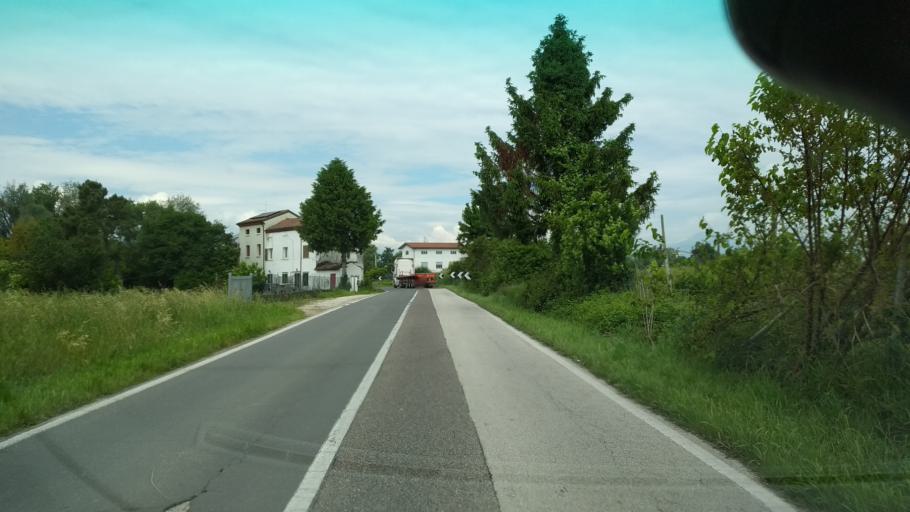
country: IT
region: Veneto
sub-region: Provincia di Vicenza
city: Monticello Conte Otto
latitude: 45.5980
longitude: 11.5497
